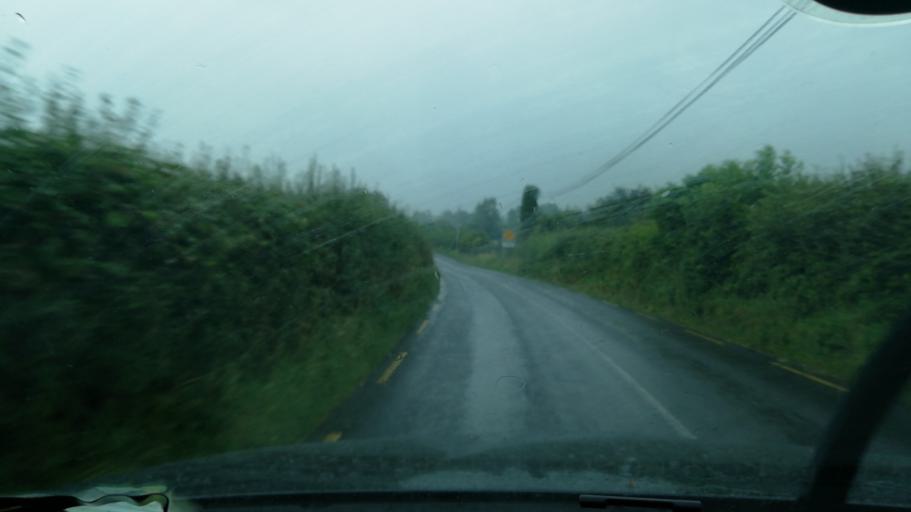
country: IE
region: Leinster
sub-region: Kilkenny
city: Kilkenny
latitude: 52.5673
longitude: -7.2773
